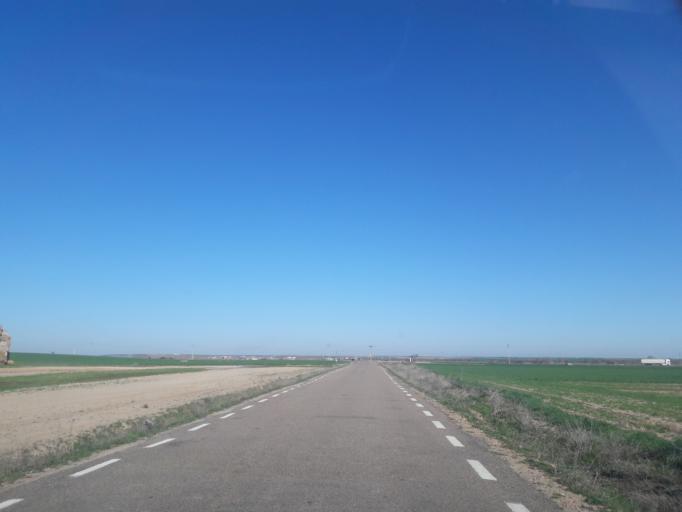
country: ES
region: Castille and Leon
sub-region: Provincia de Salamanca
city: Coca de Alba
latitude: 40.8682
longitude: -5.3742
